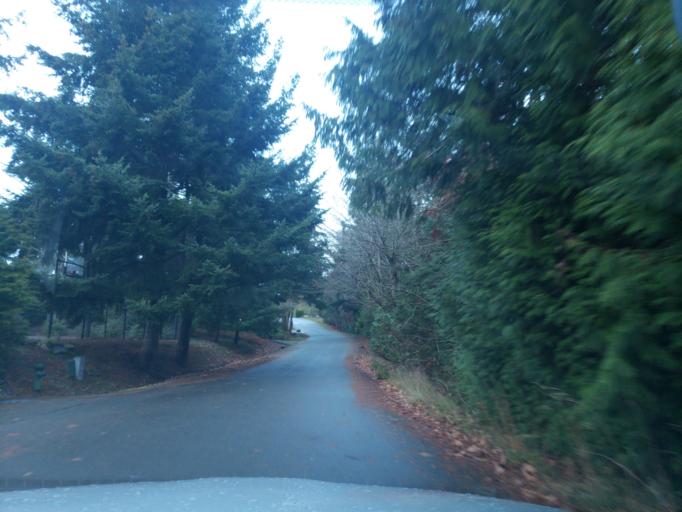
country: US
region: Washington
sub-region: Snohomish County
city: Woodway
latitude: 47.7633
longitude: -122.3805
